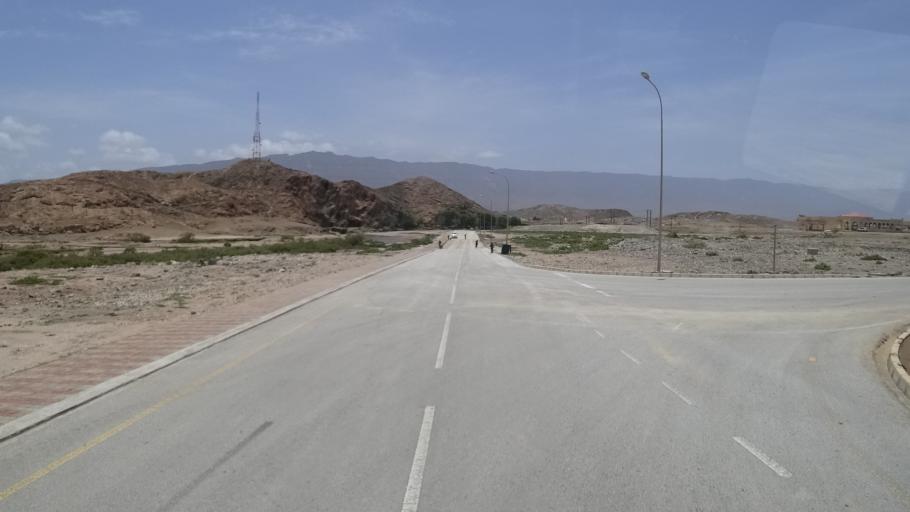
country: OM
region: Zufar
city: Salalah
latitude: 16.9970
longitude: 54.6916
